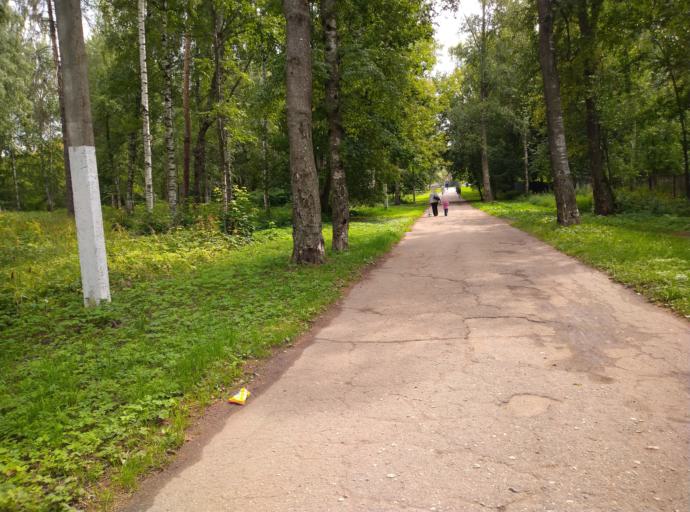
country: RU
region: Kostroma
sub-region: Kostromskoy Rayon
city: Kostroma
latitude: 57.7810
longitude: 40.9609
